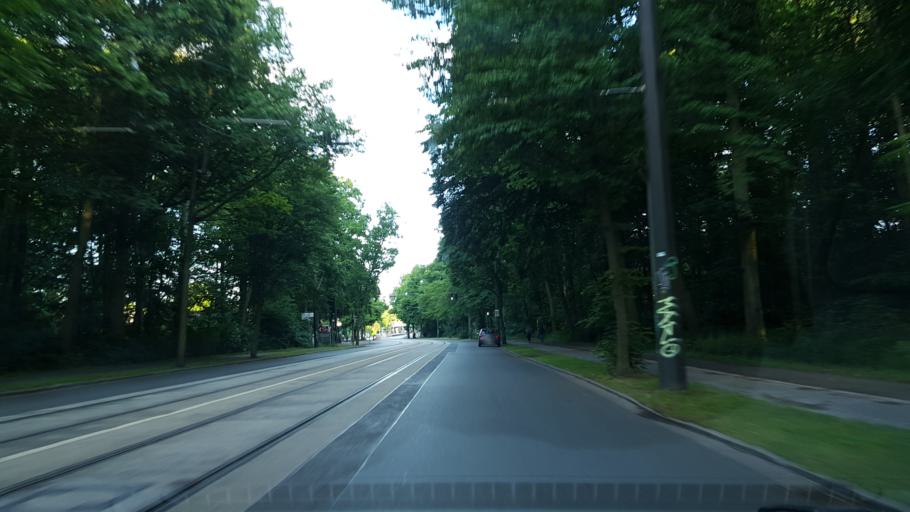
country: DE
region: Lower Saxony
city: Laatzen
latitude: 52.3680
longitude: 9.8107
